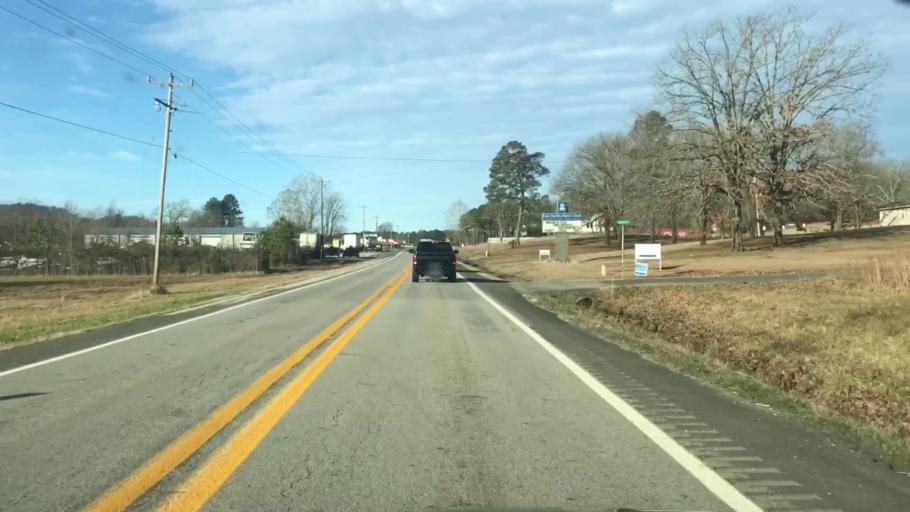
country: US
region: Arkansas
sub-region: Montgomery County
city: Mount Ida
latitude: 34.5312
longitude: -93.5243
